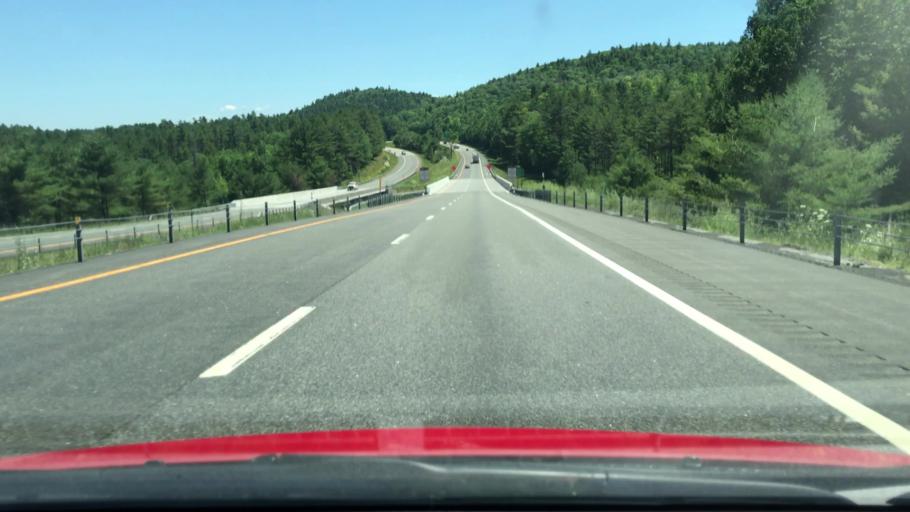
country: US
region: New York
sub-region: Essex County
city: Elizabethtown
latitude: 44.1966
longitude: -73.5311
